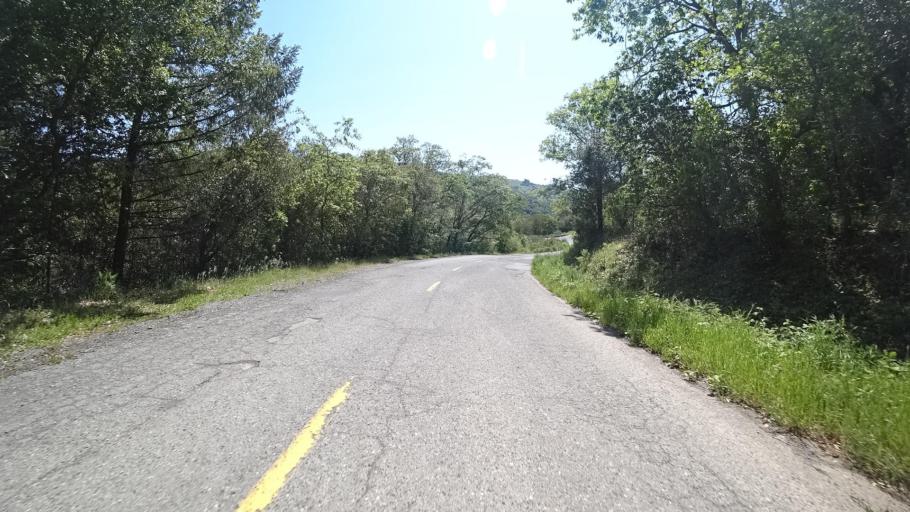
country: US
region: California
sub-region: Humboldt County
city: Redway
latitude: 40.1739
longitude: -123.6058
